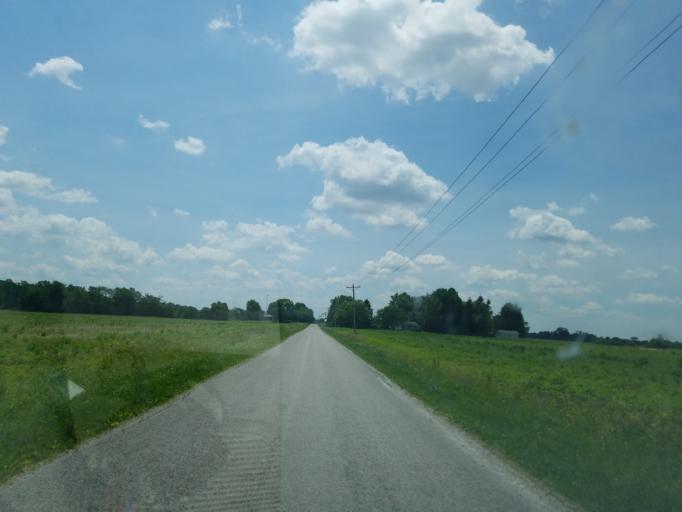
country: US
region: Ohio
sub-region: Marion County
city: Marion
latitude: 40.6269
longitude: -82.9910
